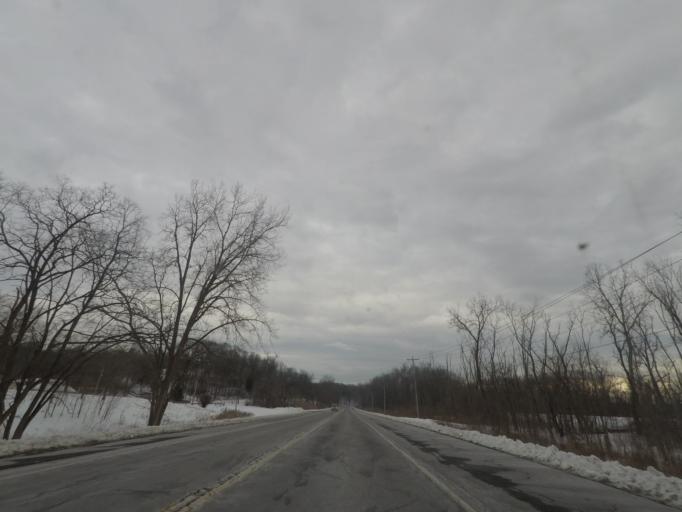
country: US
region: New York
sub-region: Rensselaer County
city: Castleton-on-Hudson
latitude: 42.5479
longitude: -73.7483
